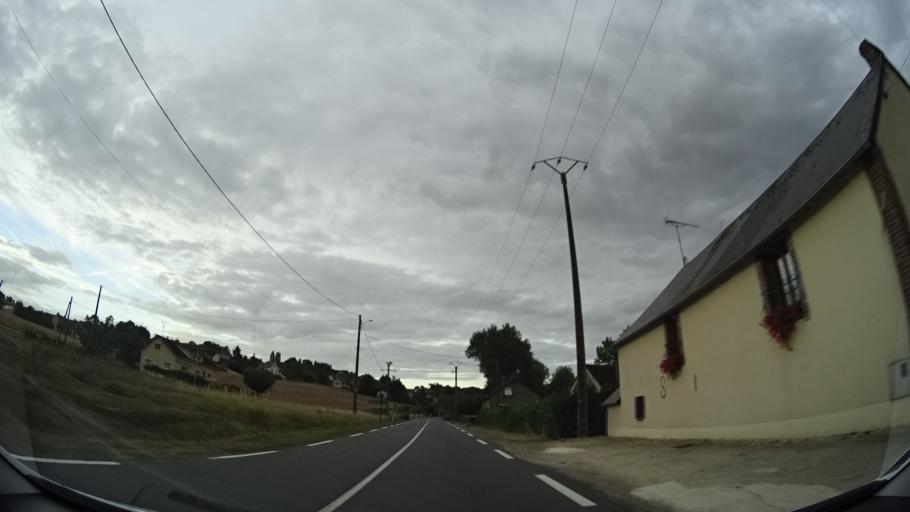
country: FR
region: Centre
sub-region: Departement du Loiret
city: Trigueres
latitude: 47.9413
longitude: 2.9931
